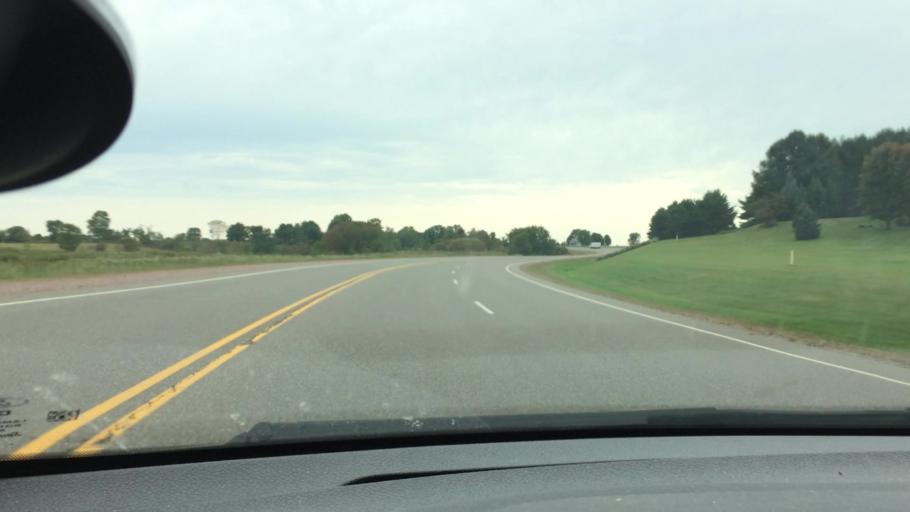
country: US
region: Wisconsin
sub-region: Clark County
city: Neillsville
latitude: 44.5552
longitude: -90.6393
